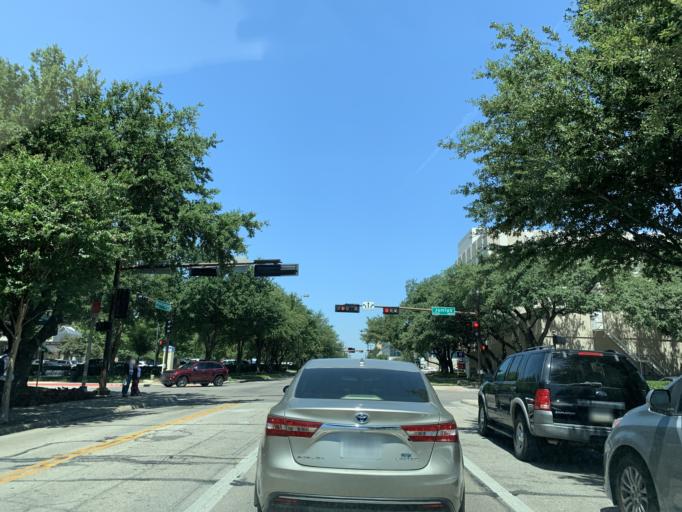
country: US
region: Texas
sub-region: Dallas County
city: Dallas
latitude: 32.7908
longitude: -96.7779
